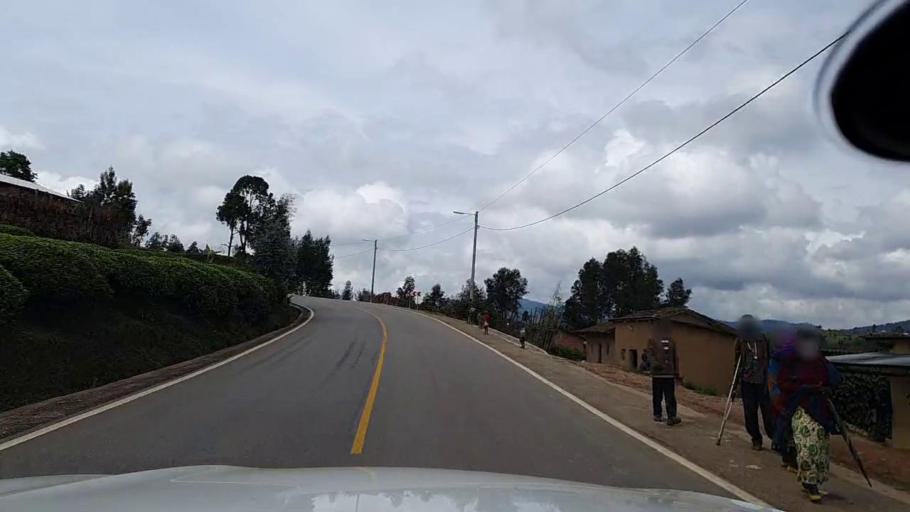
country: RW
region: Southern Province
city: Nzega
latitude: -2.5249
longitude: 29.4522
